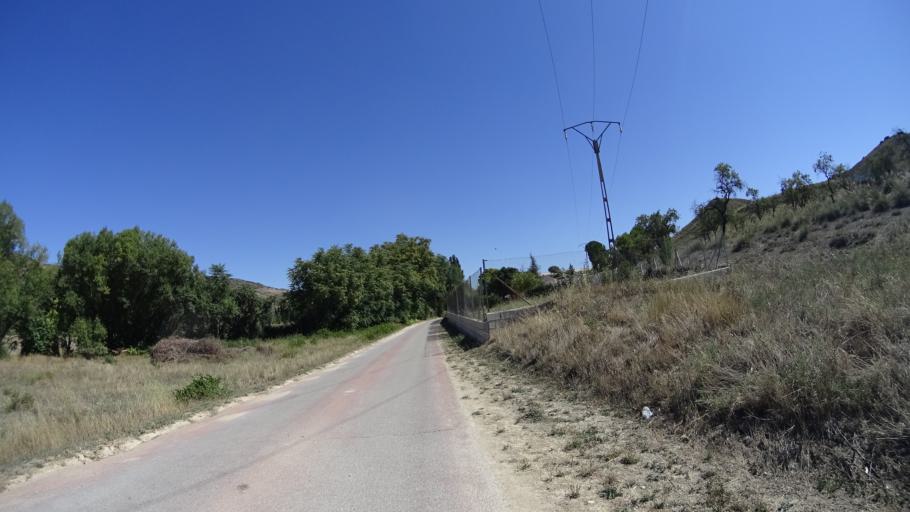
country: ES
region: Madrid
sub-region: Provincia de Madrid
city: Perales de Tajuna
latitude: 40.2285
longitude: -3.3282
